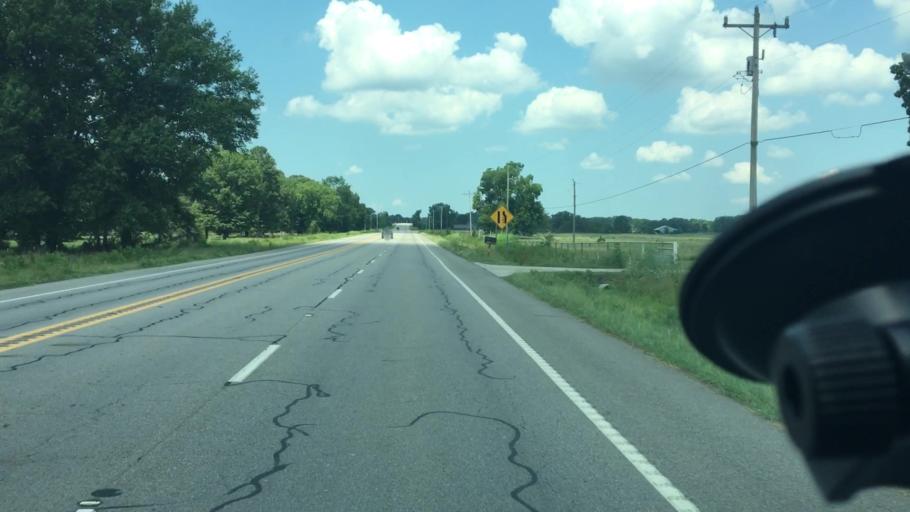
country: US
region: Arkansas
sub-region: Logan County
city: Paris
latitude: 35.2985
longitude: -93.8157
